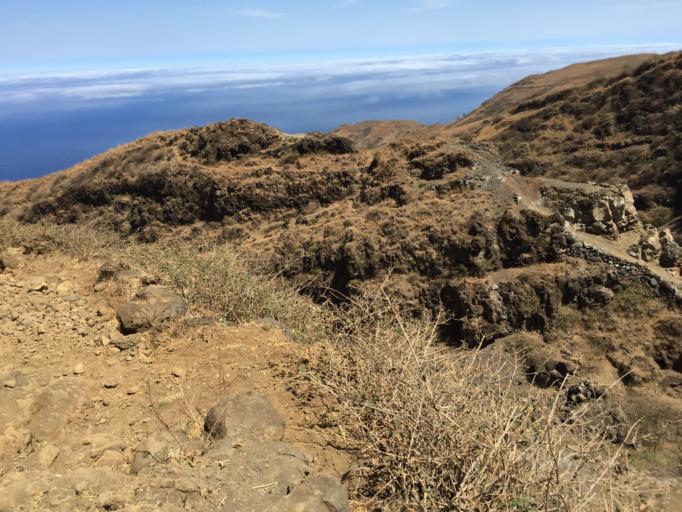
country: CV
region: Mosteiros
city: Porto dos Mosteiros
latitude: 15.0084
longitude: -24.3915
